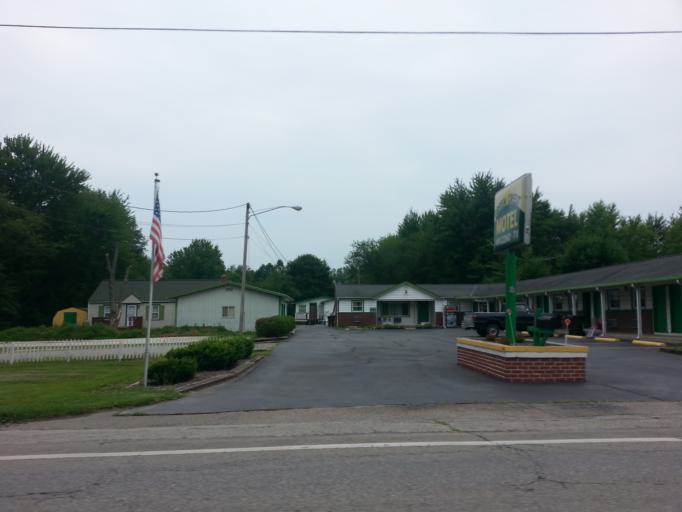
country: US
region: Ohio
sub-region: Brown County
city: Mount Orab
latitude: 39.0136
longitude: -83.9245
